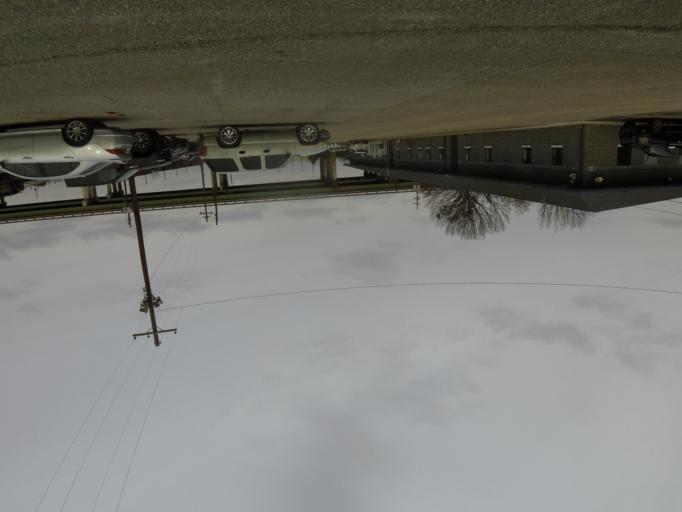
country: US
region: Alabama
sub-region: Montgomery County
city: Montgomery
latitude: 32.3954
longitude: -86.3144
